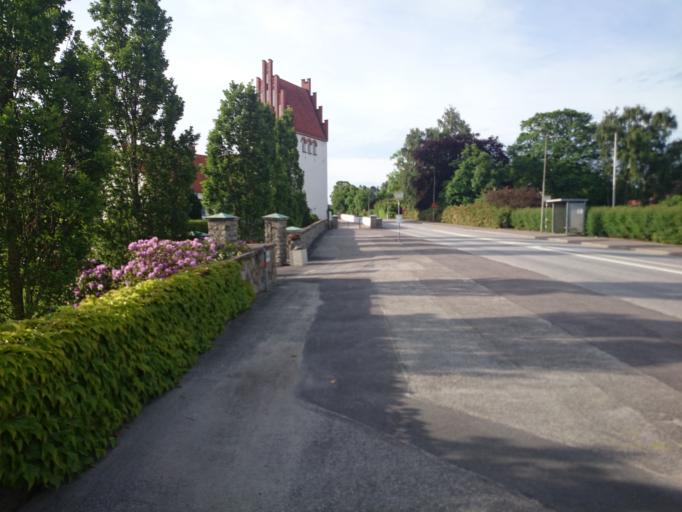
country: SE
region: Skane
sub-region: Eslovs Kommun
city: Eslov
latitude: 55.7225
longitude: 13.3405
